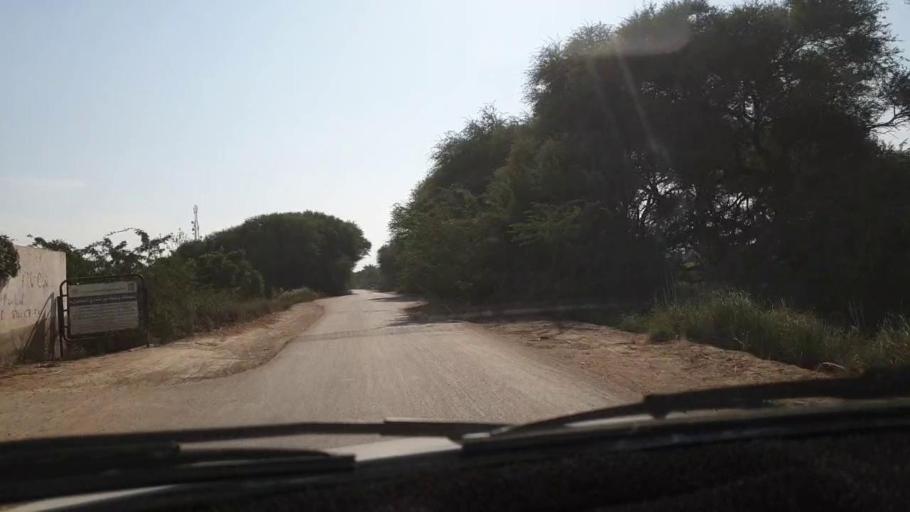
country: PK
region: Sindh
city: Bulri
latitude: 24.9623
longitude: 68.4205
